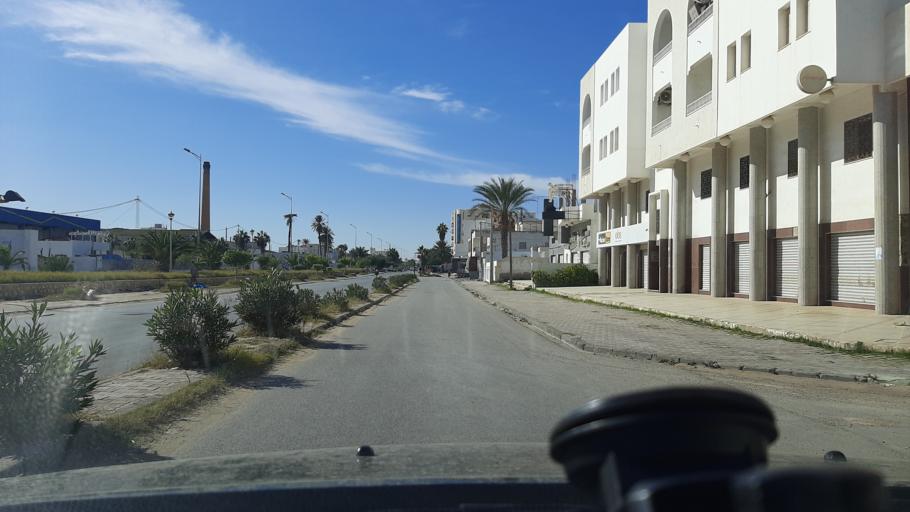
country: TN
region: Safaqis
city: Sfax
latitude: 34.7264
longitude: 10.7409
